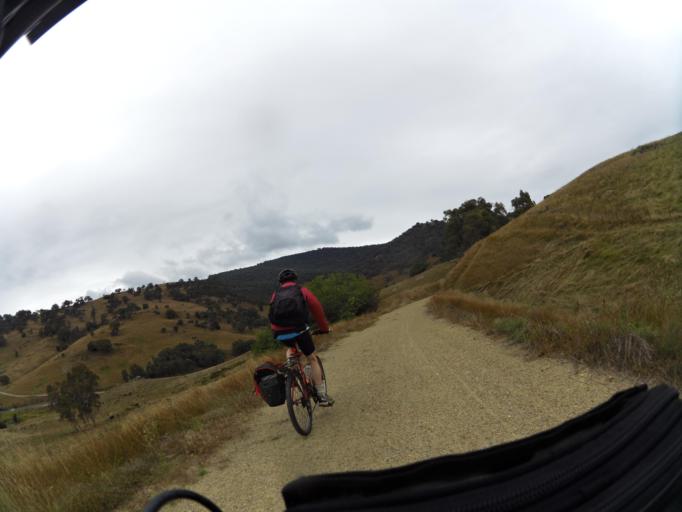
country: AU
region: New South Wales
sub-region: Albury Municipality
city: East Albury
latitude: -36.1864
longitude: 147.3656
